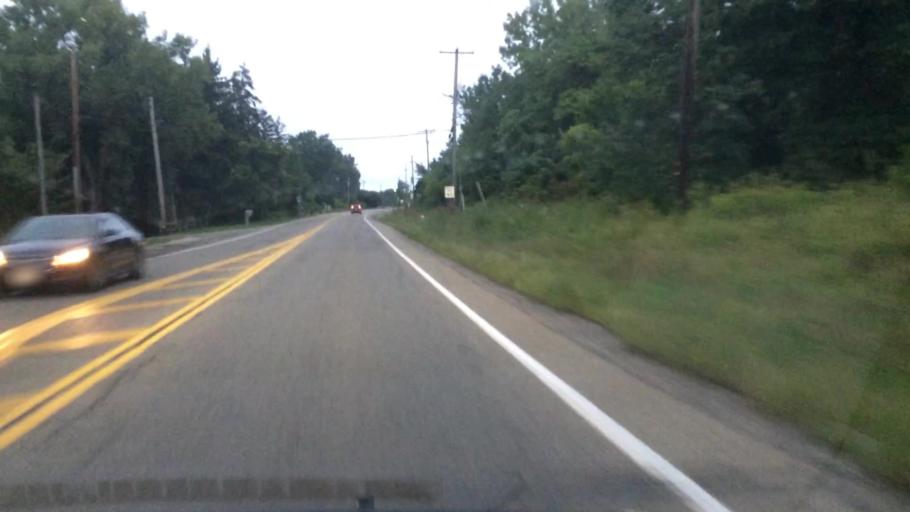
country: US
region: Ohio
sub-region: Summit County
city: Silver Lake
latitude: 41.2047
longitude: -81.4952
